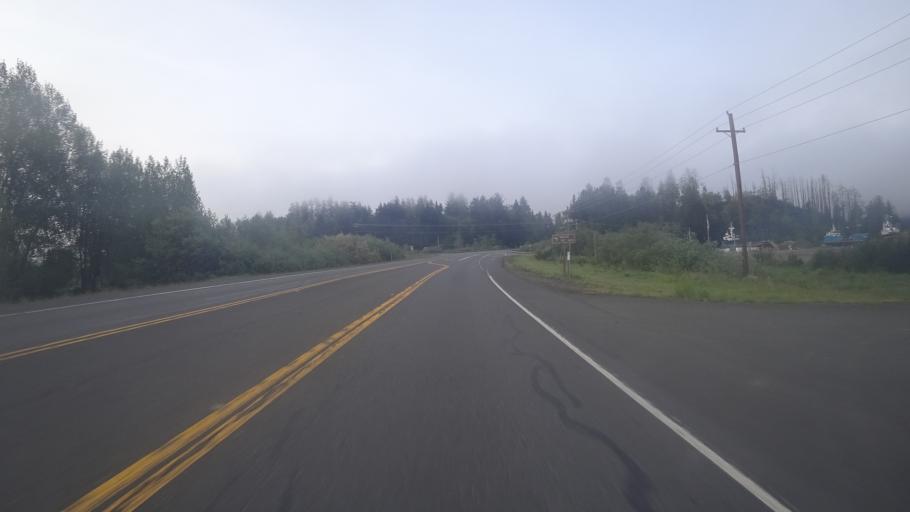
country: US
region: Oregon
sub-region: Douglas County
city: Reedsport
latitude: 43.7157
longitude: -124.0990
